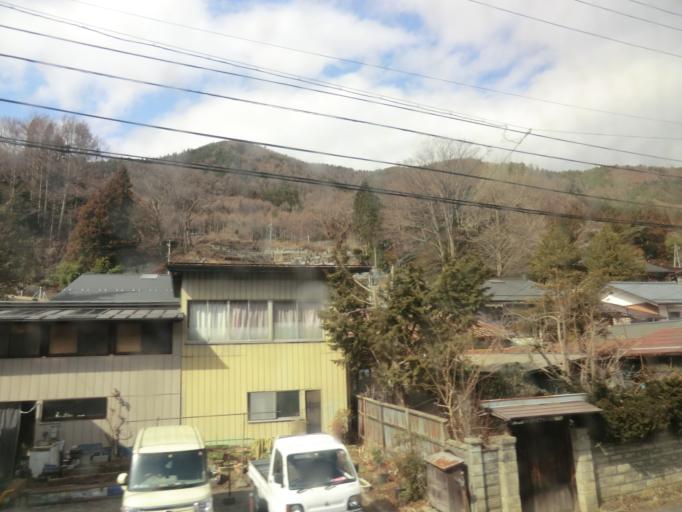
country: JP
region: Nagano
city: Tatsuno
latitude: 35.9674
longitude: 137.8141
